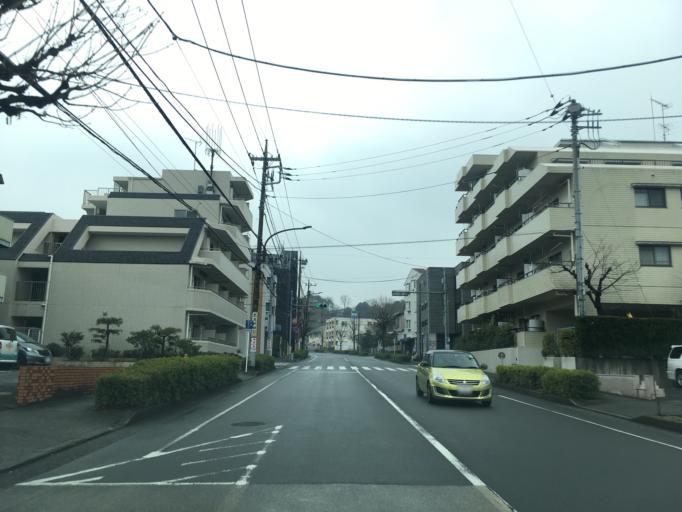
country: JP
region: Tokyo
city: Hino
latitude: 35.6208
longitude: 139.4287
